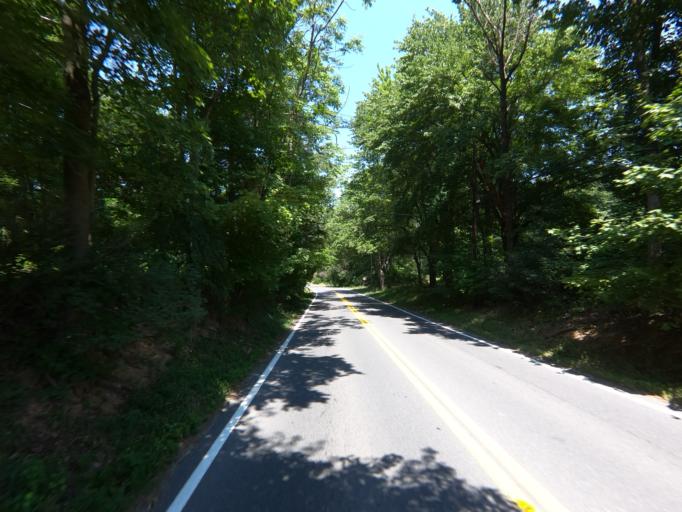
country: US
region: Maryland
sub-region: Montgomery County
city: Clarksburg
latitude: 39.2601
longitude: -77.3027
